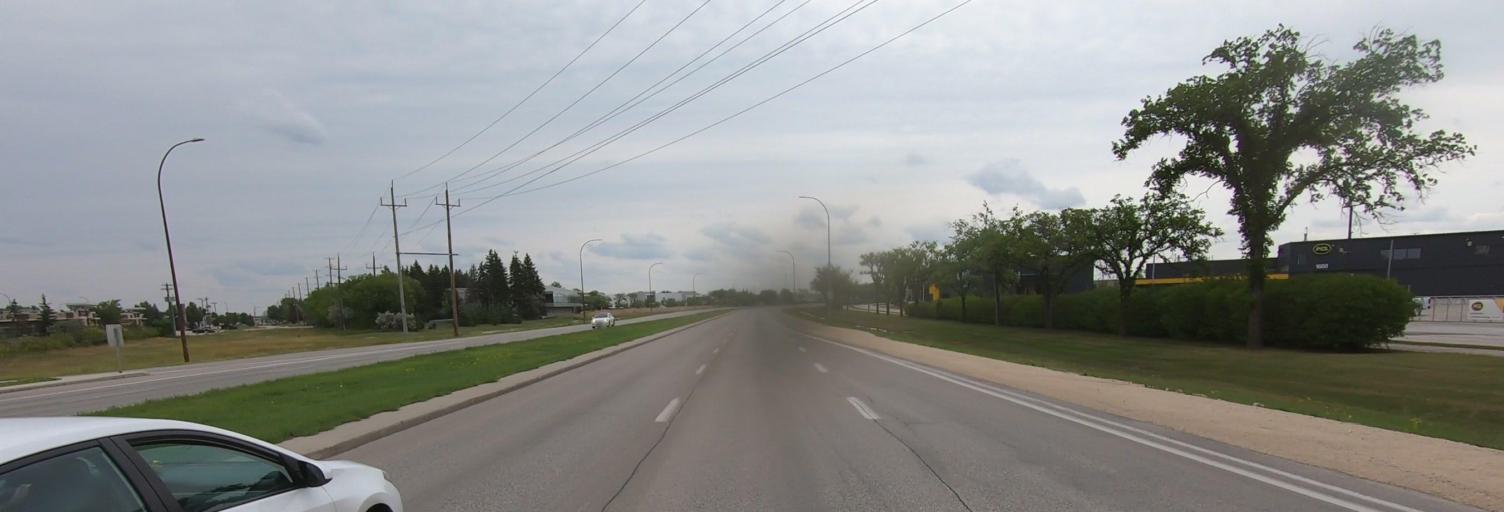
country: CA
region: Manitoba
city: Winnipeg
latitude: 49.8306
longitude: -97.1794
